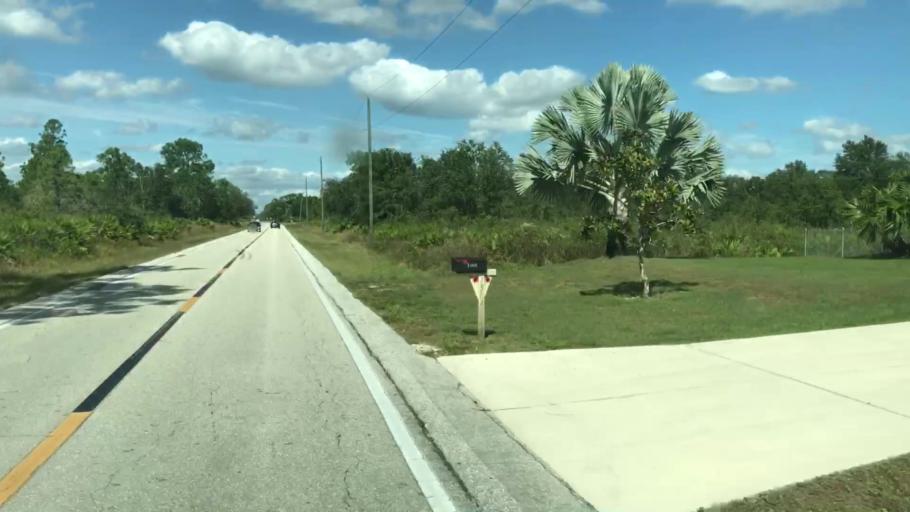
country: US
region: Florida
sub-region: Lee County
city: Lehigh Acres
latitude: 26.6554
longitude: -81.6255
